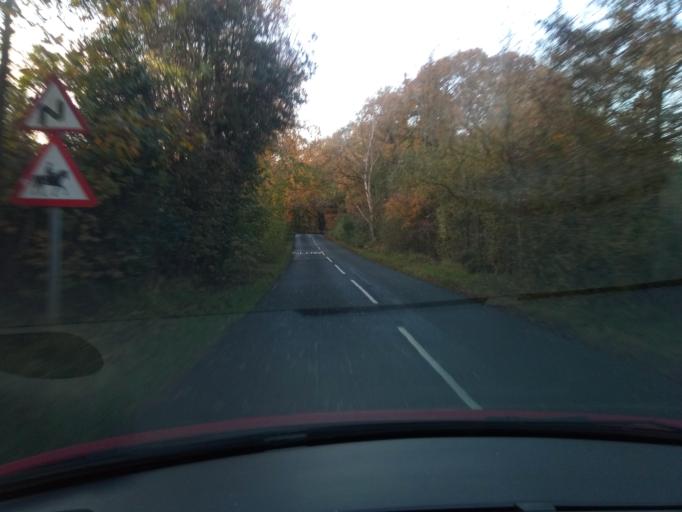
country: GB
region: England
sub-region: County Durham
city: Hamsterley
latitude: 54.6788
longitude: -1.8414
